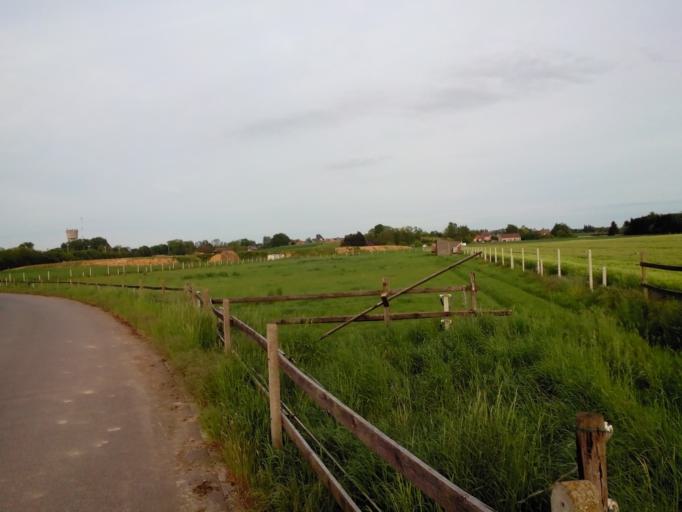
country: BE
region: Flanders
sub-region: Provincie Vlaams-Brabant
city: Leuven
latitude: 50.8431
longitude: 4.7173
